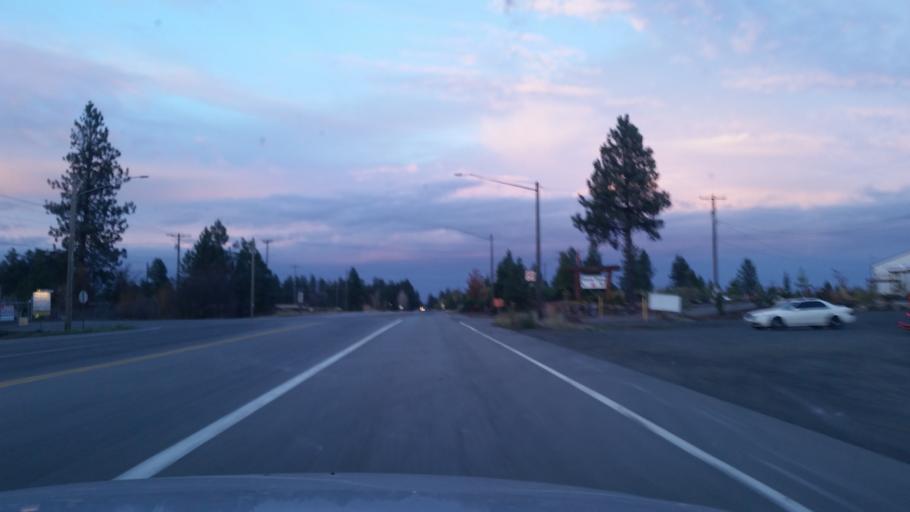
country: US
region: Washington
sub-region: Spokane County
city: Spokane
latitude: 47.6274
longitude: -117.5005
